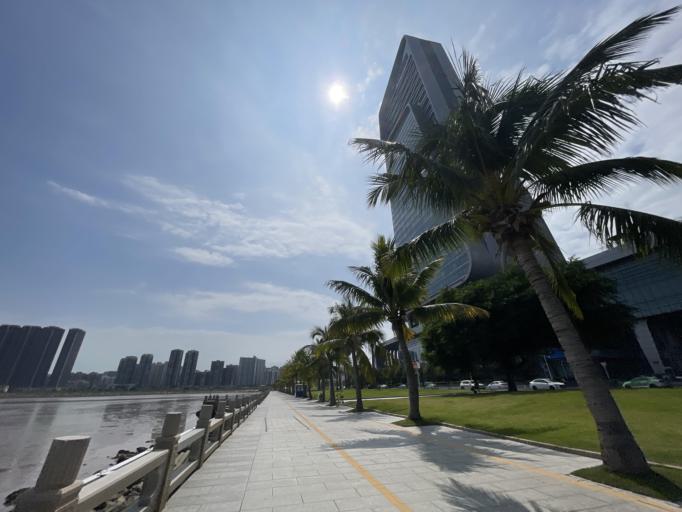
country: MO
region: Macau
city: Macau
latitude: 22.2223
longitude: 113.5547
